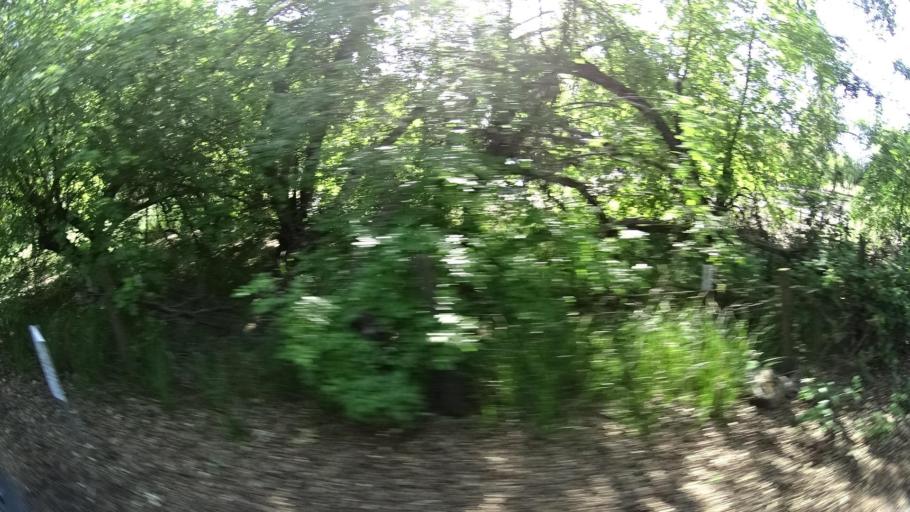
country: US
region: California
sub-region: Lake County
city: Kelseyville
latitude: 39.0214
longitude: -122.8475
